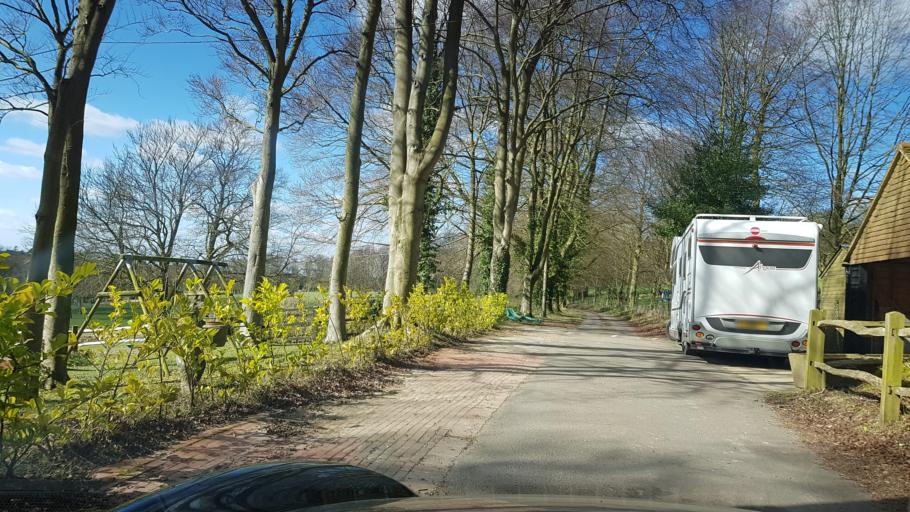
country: GB
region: England
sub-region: Surrey
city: Godalming
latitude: 51.2253
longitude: -0.6334
